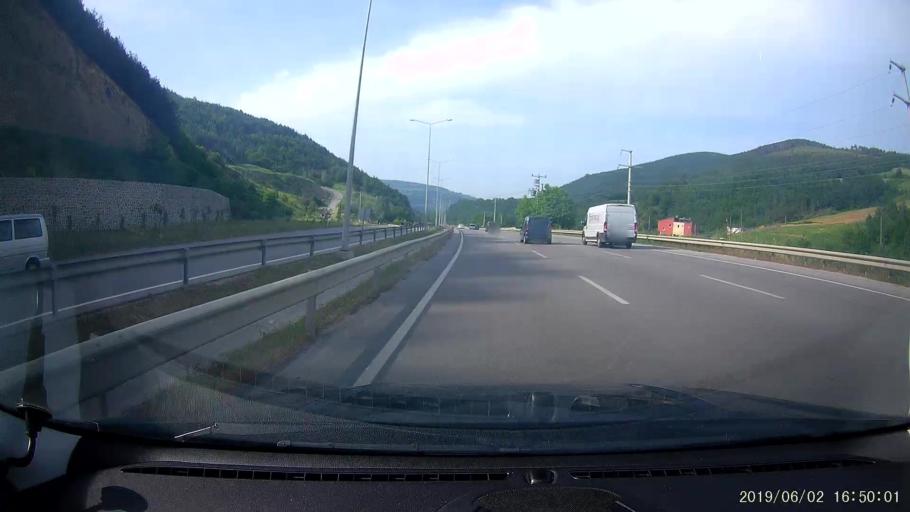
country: TR
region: Samsun
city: Samsun
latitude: 41.2459
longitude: 36.1725
